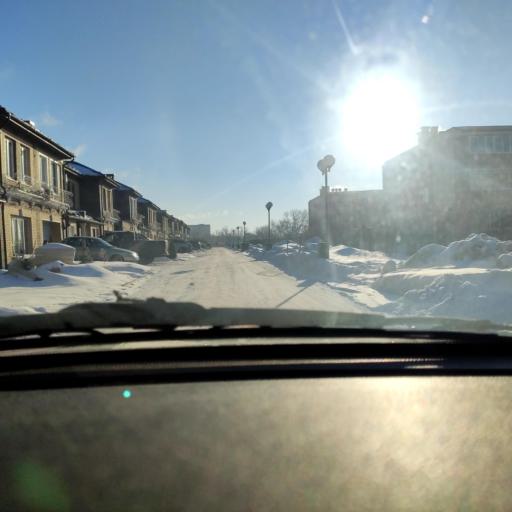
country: RU
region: Samara
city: Tol'yatti
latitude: 53.5045
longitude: 49.2482
